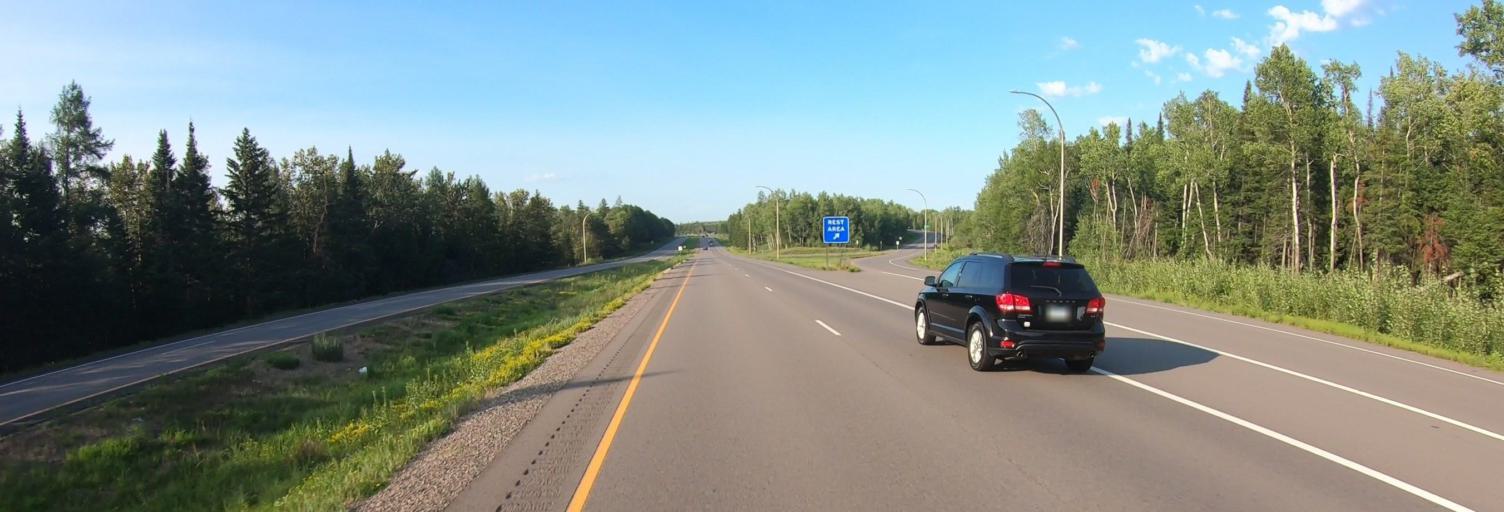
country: US
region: Minnesota
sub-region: Saint Louis County
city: Eveleth
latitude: 47.3149
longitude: -92.4743
